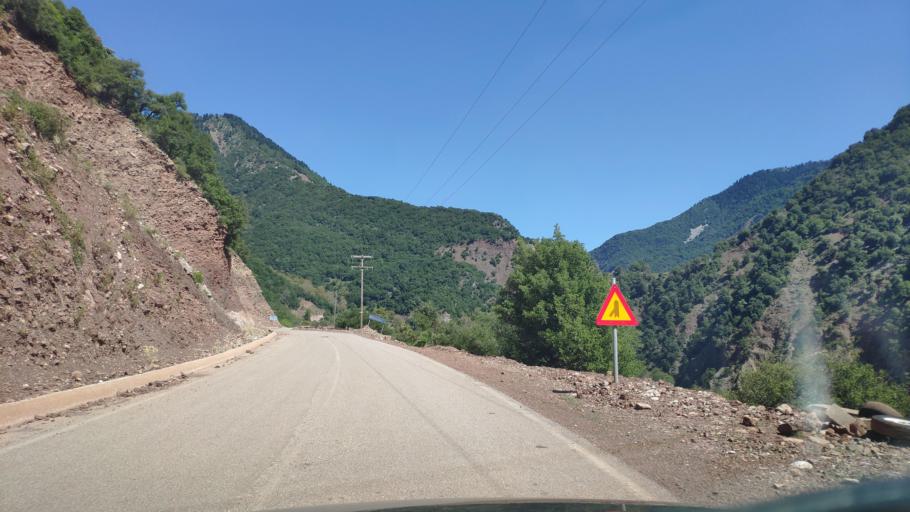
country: GR
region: Central Greece
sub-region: Nomos Evrytanias
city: Kerasochori
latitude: 39.0818
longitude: 21.5966
